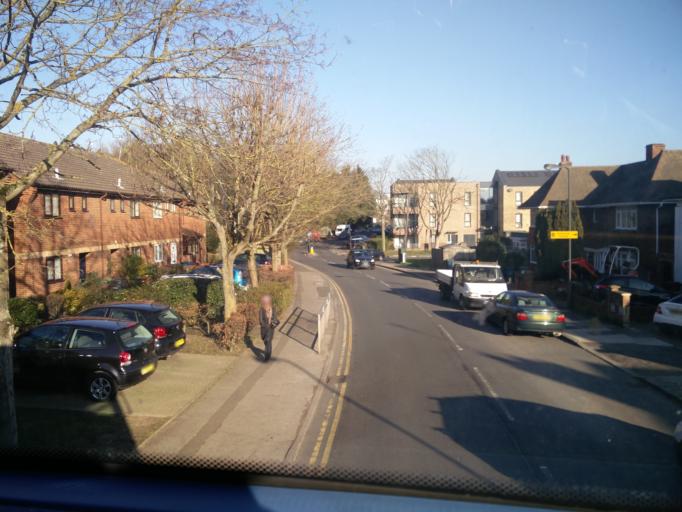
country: GB
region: England
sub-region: Greater London
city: Northolt
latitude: 51.5689
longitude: -0.3635
